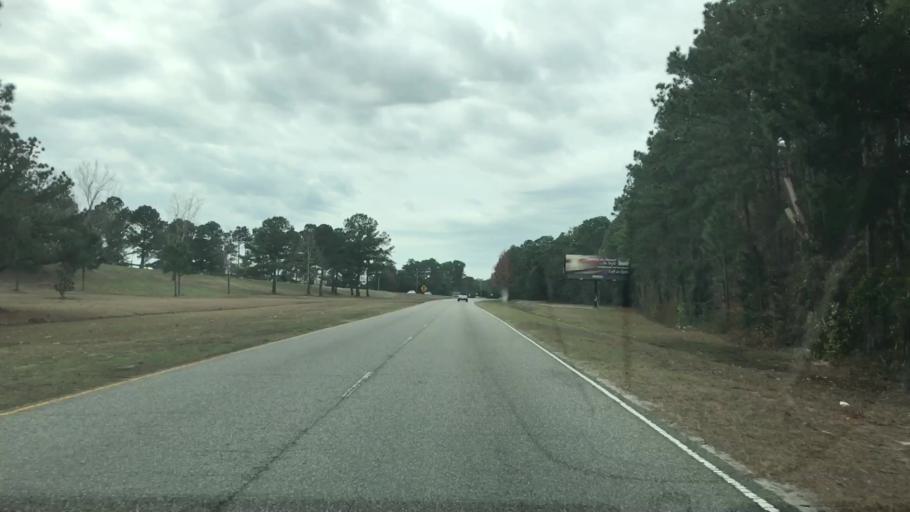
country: US
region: South Carolina
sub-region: Horry County
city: Myrtle Beach
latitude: 33.7683
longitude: -78.8062
